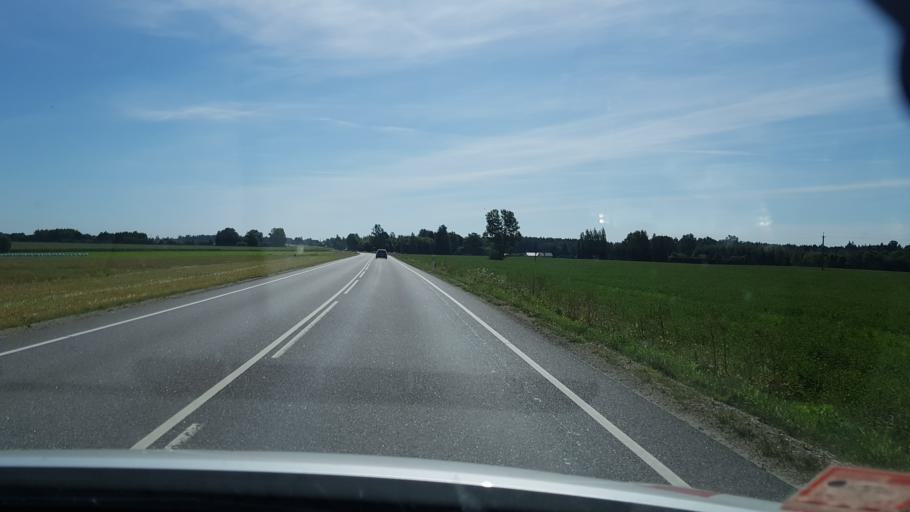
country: EE
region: Tartu
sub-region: Tartu linn
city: Tartu
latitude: 58.4283
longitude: 26.8494
